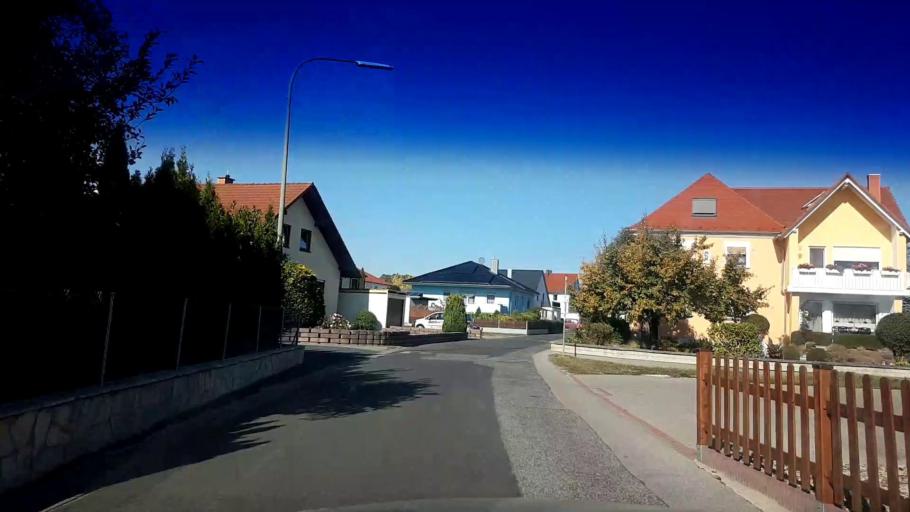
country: DE
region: Bavaria
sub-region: Upper Franconia
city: Oberhaid
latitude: 49.9335
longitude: 10.8120
